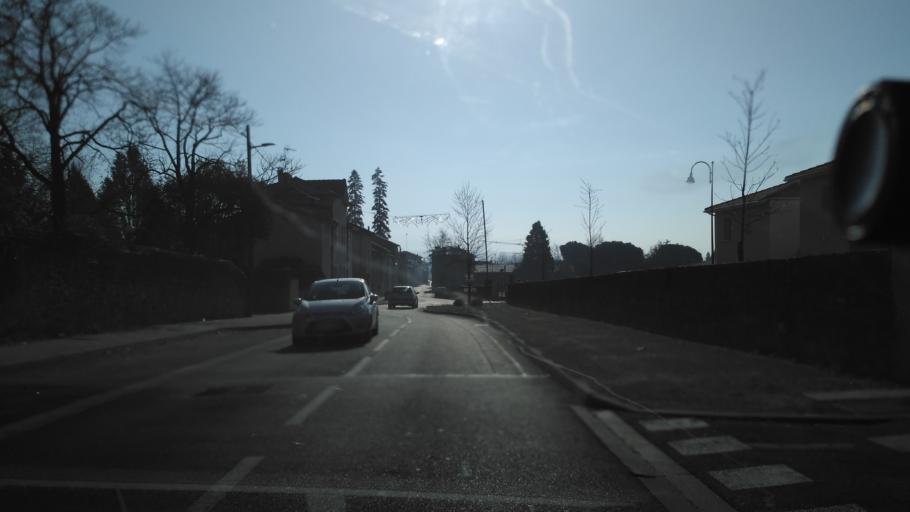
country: FR
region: Rhone-Alpes
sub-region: Departement de la Drome
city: Genissieux
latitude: 45.0869
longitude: 5.0858
